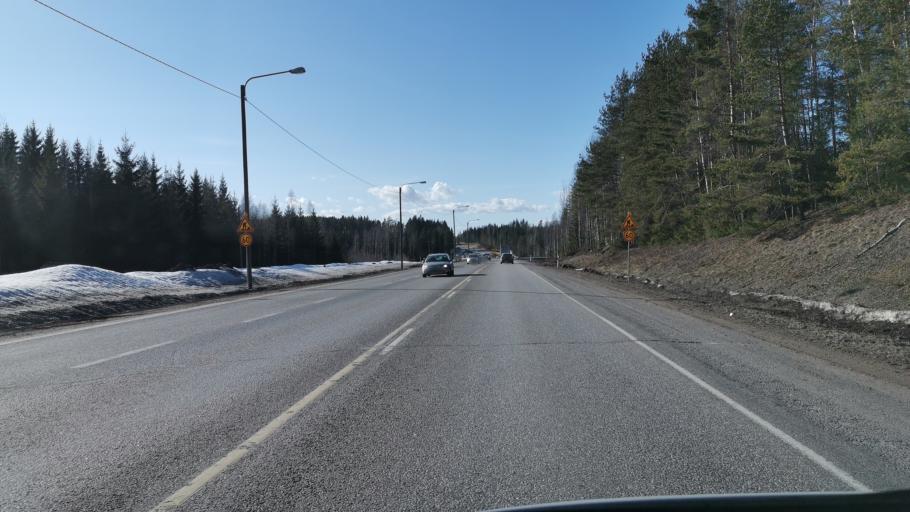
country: FI
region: Kymenlaakso
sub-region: Kouvola
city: Kouvola
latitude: 60.8669
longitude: 26.5574
